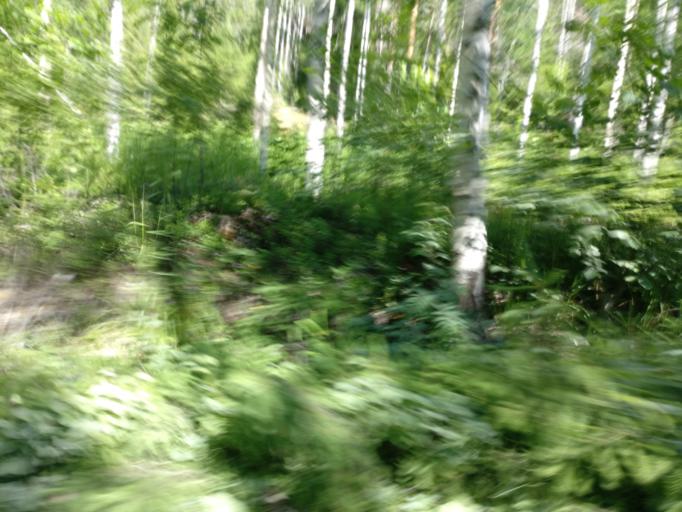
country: FI
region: Northern Savo
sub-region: Varkaus
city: Kangaslampi
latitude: 62.1746
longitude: 28.2397
